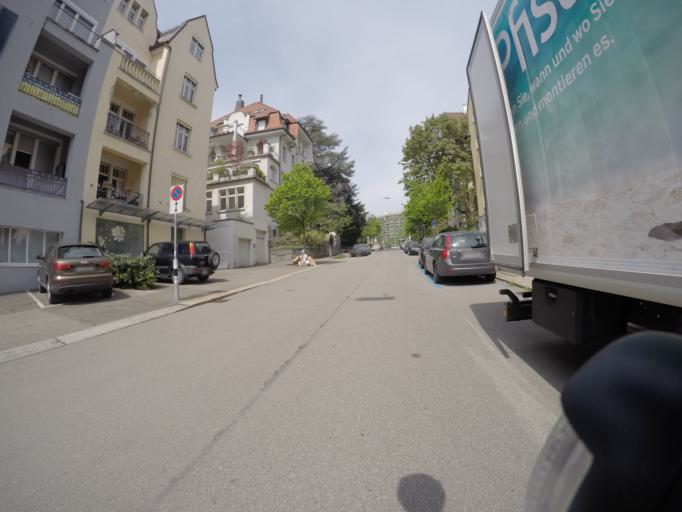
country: CH
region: Zurich
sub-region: Bezirk Zuerich
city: Zuerich (Kreis 6) / Oberstrass
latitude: 47.3864
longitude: 8.5454
